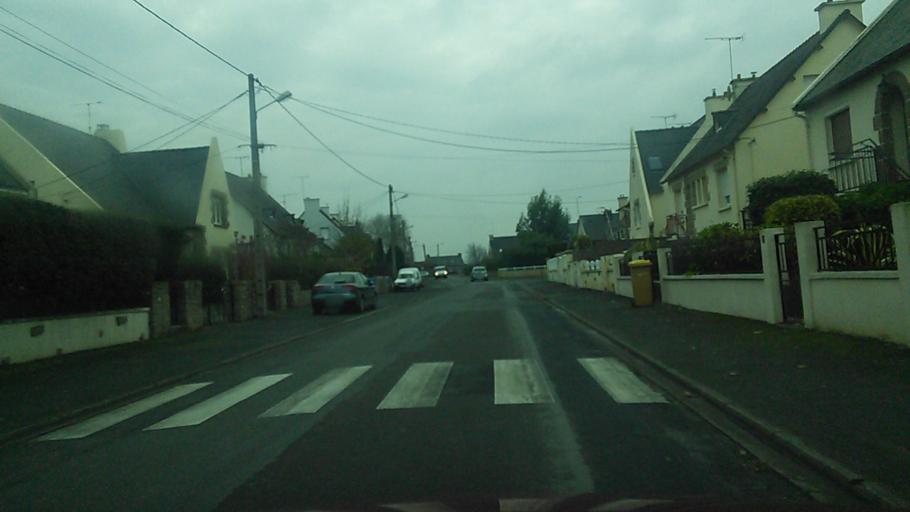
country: FR
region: Brittany
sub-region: Departement des Cotes-d'Armor
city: Pommeret
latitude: 48.4870
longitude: -2.6438
